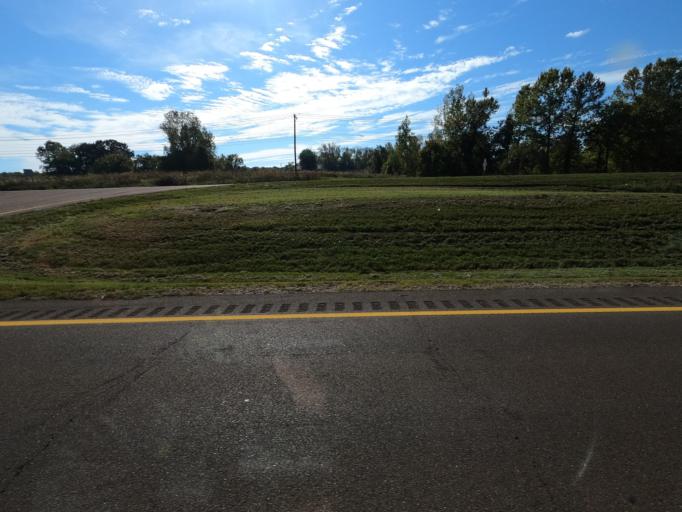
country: US
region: Tennessee
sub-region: Tipton County
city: Atoka
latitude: 35.4635
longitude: -89.7636
